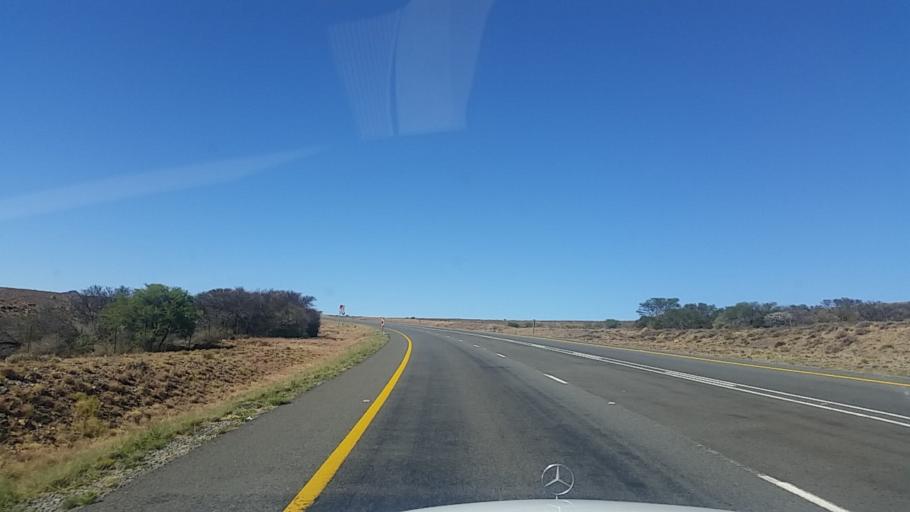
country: ZA
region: Eastern Cape
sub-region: Cacadu District Municipality
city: Graaff-Reinet
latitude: -31.9480
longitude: 24.7259
